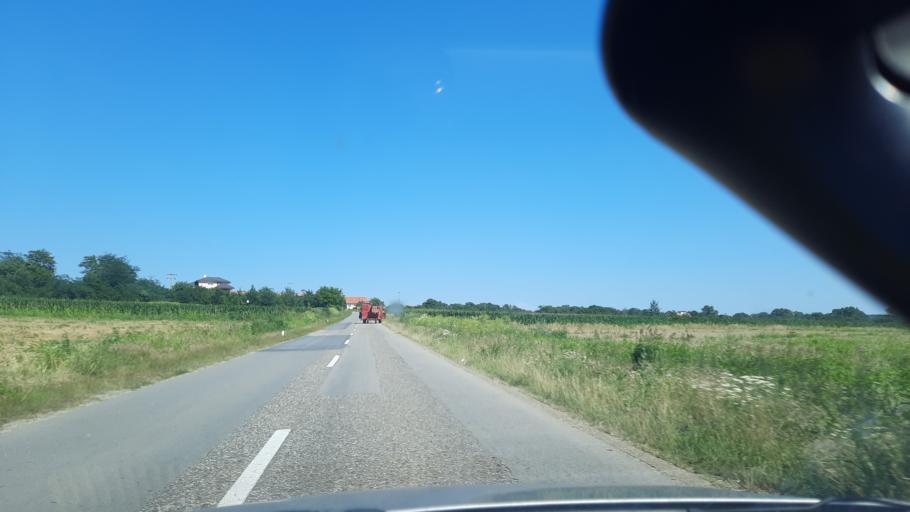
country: RS
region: Central Serbia
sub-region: Branicevski Okrug
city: Malo Crnice
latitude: 44.5741
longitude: 21.3536
